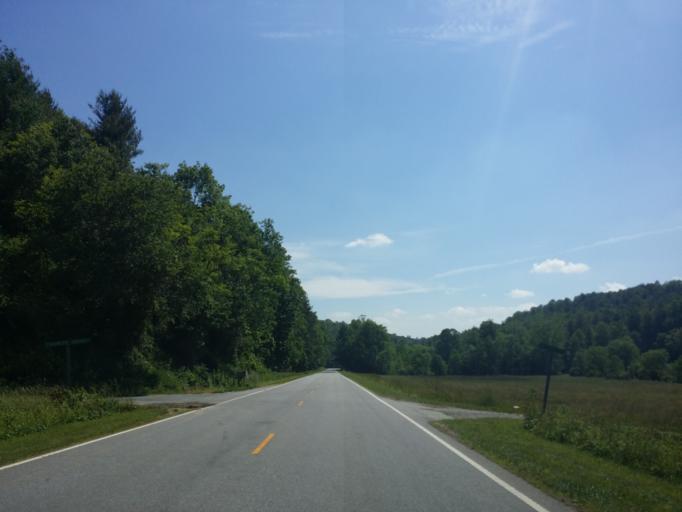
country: US
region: North Carolina
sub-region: Madison County
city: Marshall
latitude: 35.7049
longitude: -82.7887
